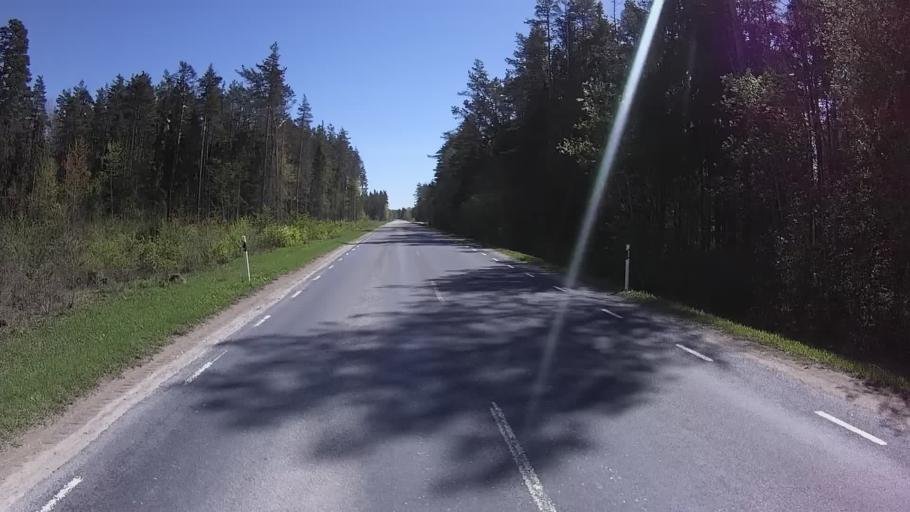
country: EE
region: Harju
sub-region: Raasiku vald
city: Raasiku
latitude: 59.1632
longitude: 25.1792
